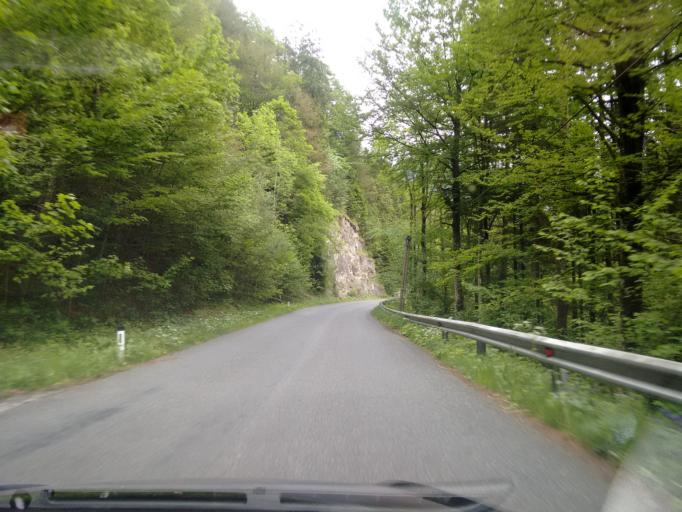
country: AT
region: Upper Austria
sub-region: Politischer Bezirk Gmunden
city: Ebensee
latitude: 47.8337
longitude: 13.7301
